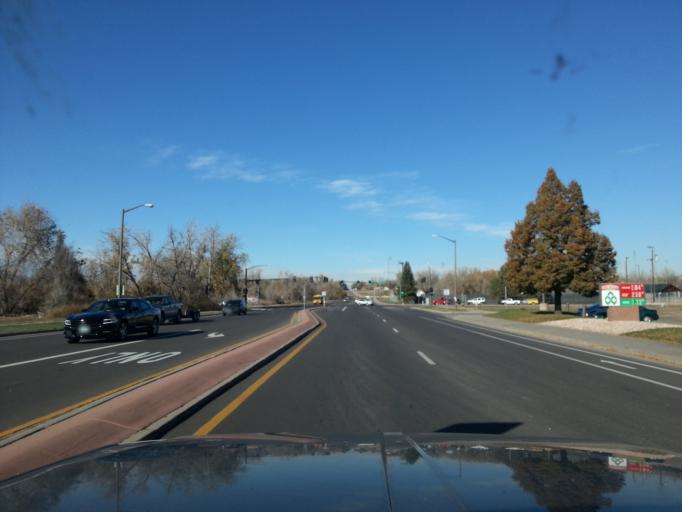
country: US
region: Colorado
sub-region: Larimer County
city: Loveland
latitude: 40.3915
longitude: -105.0968
